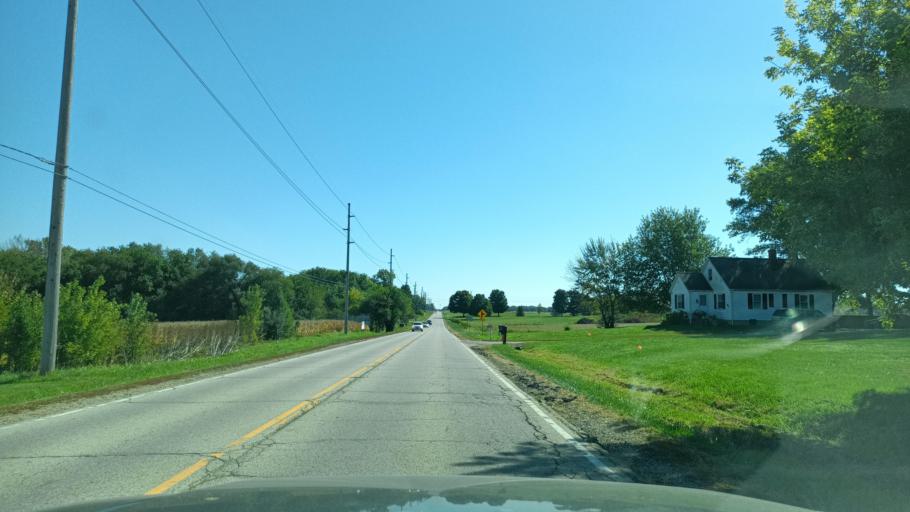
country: US
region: Illinois
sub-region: Peoria County
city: Dunlap
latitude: 40.7837
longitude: -89.7132
